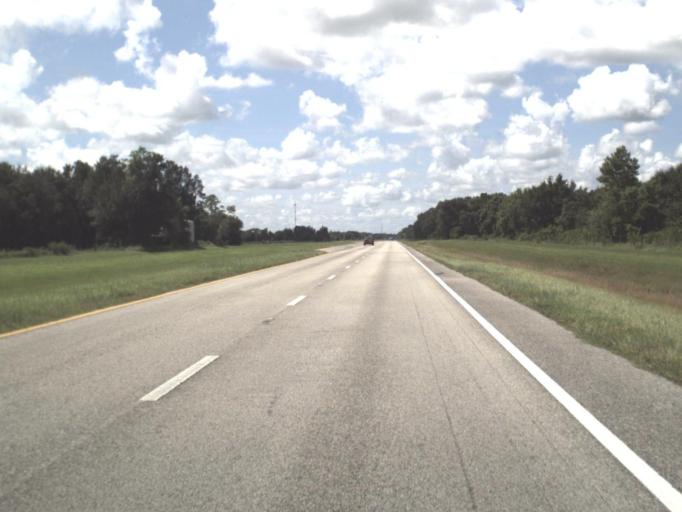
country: US
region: Florida
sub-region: DeSoto County
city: Arcadia
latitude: 27.2773
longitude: -81.8331
